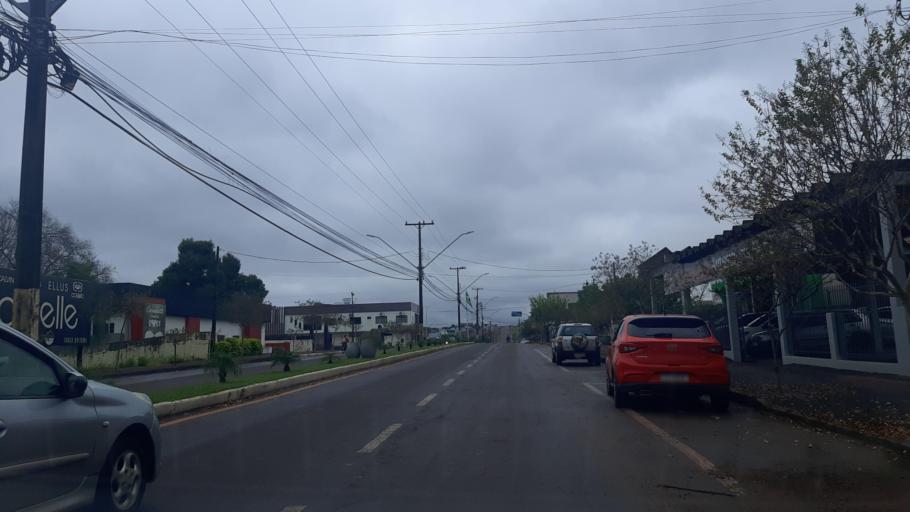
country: BR
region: Parana
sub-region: Santo Antonio Do Sudoeste
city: Santo Antonio do Sudoeste
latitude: -26.0602
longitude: -53.7262
